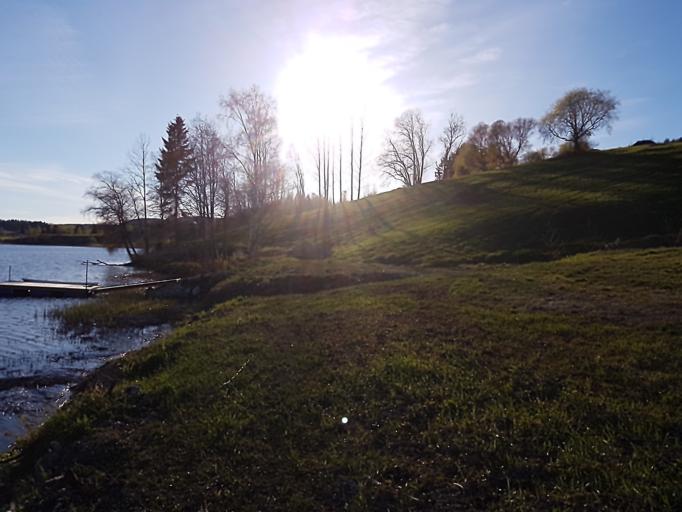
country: SE
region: Vaesternorrland
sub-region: Sundsvalls Kommun
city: Vi
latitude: 62.3232
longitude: 17.2171
